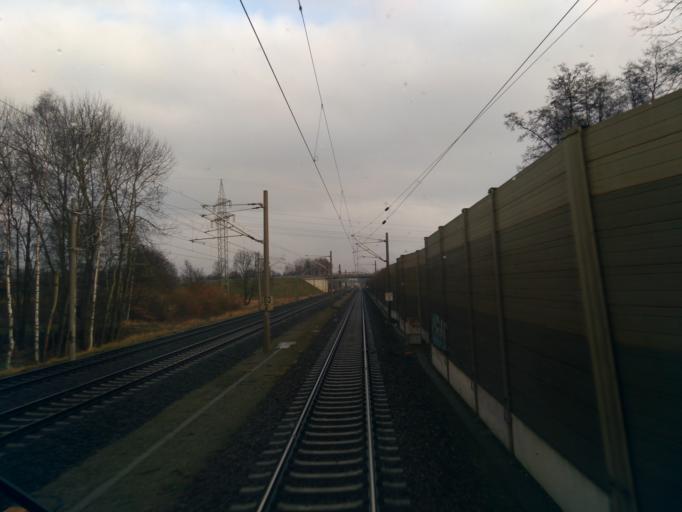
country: DE
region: Lower Saxony
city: Winsen
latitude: 53.3598
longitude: 10.1829
